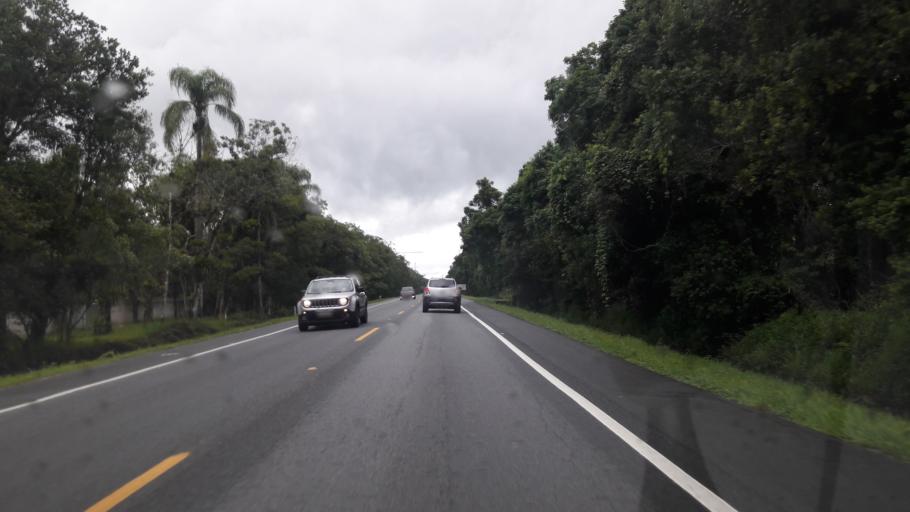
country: BR
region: Parana
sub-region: Pontal Do Parana
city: Pontal do Parana
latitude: -25.6534
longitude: -48.5247
